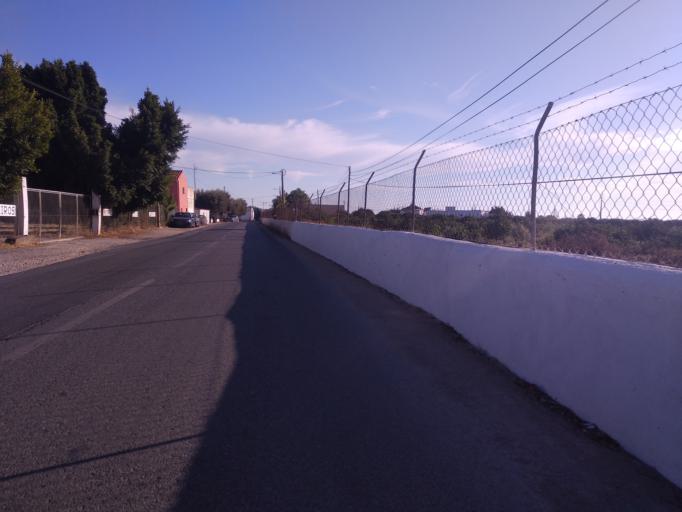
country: PT
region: Faro
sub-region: Faro
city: Faro
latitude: 37.0476
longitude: -7.9377
